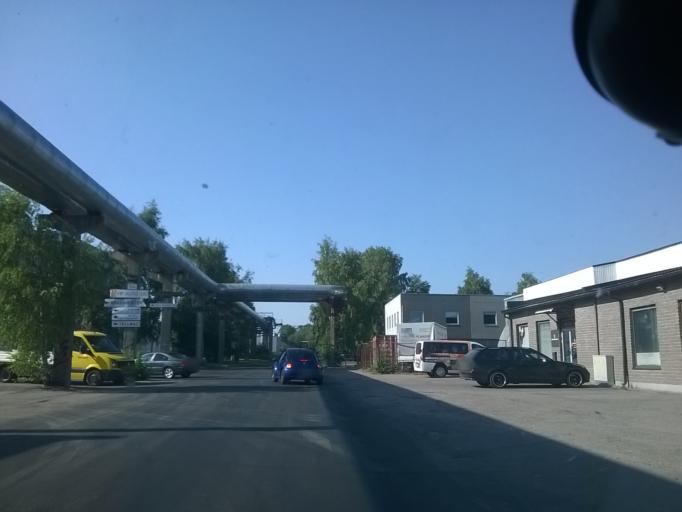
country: EE
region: Harju
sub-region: Tallinna linn
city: Tallinn
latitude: 59.4192
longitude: 24.6874
